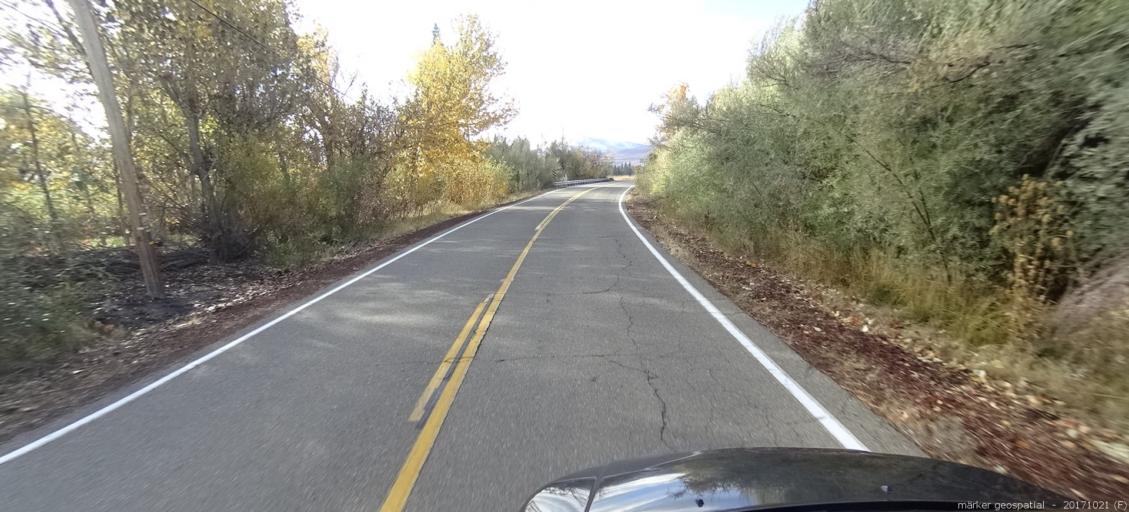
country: US
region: California
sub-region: Shasta County
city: Burney
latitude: 40.9001
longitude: -121.5471
